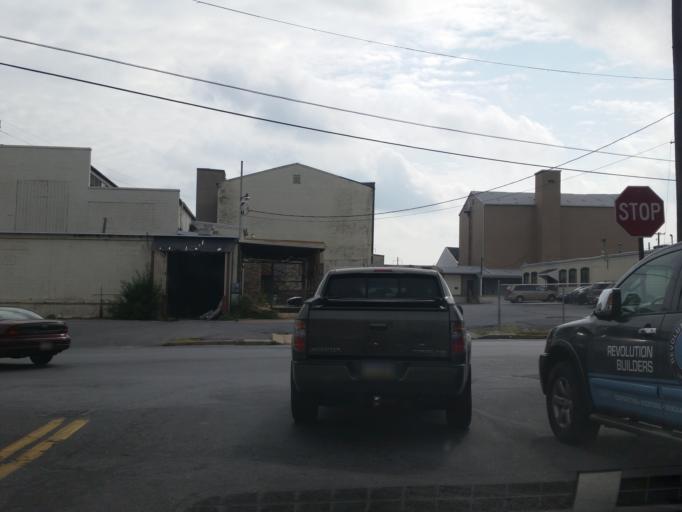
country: US
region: Pennsylvania
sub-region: Lancaster County
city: Lancaster
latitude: 40.0530
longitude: -76.2999
